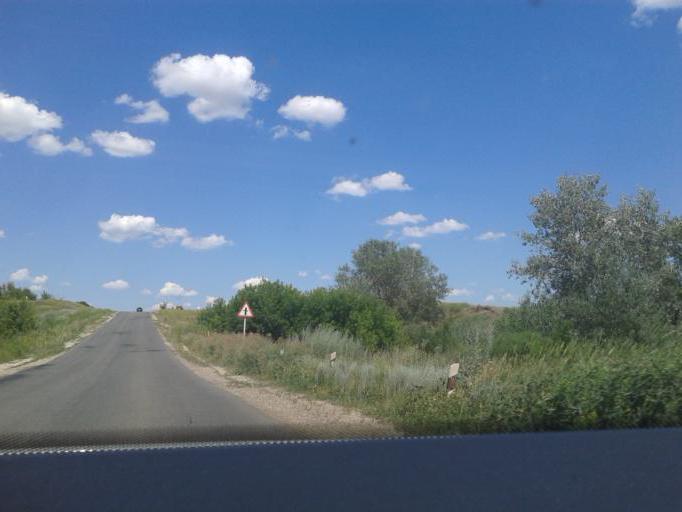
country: RU
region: Volgograd
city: Frolovo
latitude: 49.6700
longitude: 43.6294
